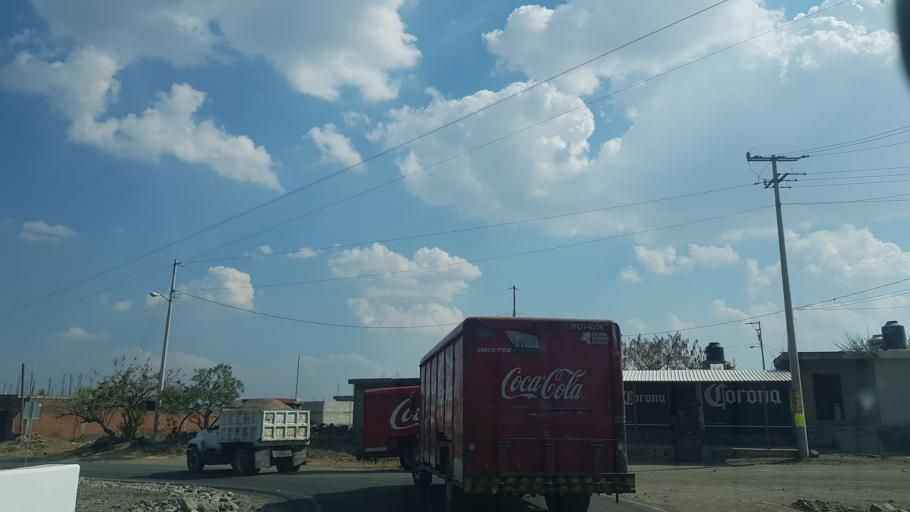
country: MX
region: Puebla
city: Atlixco
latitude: 18.9121
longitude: -98.4778
